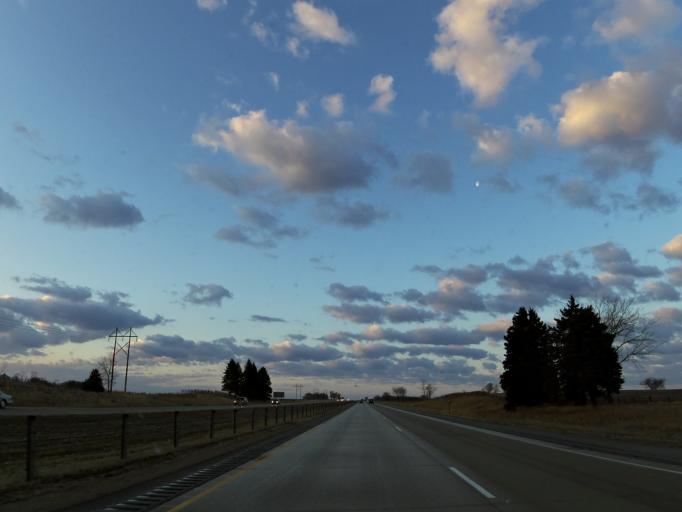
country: US
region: Minnesota
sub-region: Rice County
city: Dundas
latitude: 44.4460
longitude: -93.2926
